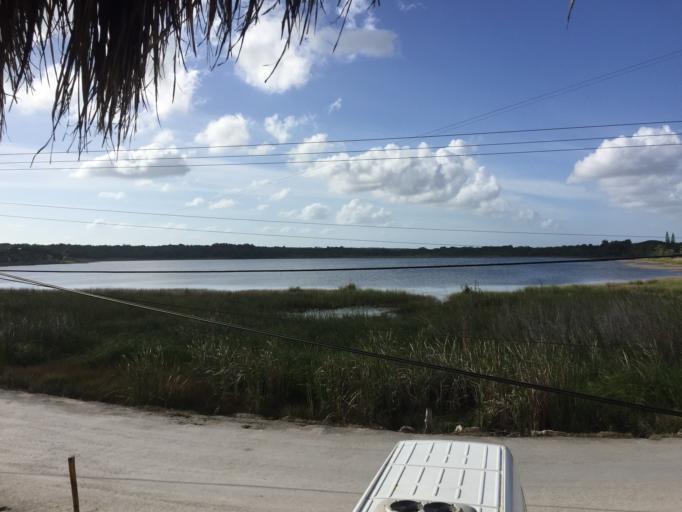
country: MX
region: Quintana Roo
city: Coba
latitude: 20.4908
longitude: -87.7337
